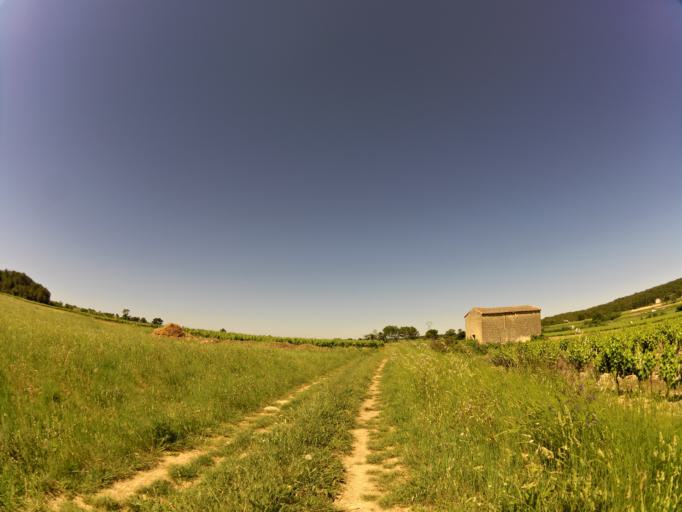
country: FR
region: Languedoc-Roussillon
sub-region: Departement du Gard
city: Mus
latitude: 43.7513
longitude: 4.1990
